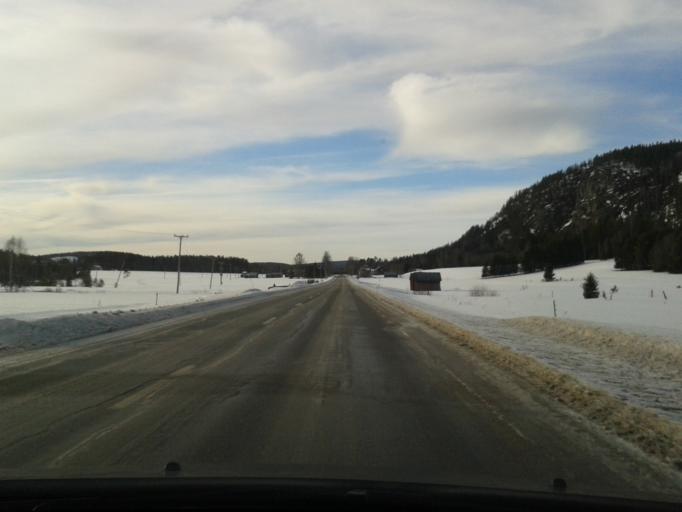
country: SE
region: Vaesternorrland
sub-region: OErnskoeldsviks Kommun
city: Bredbyn
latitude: 63.5268
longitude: 18.0181
